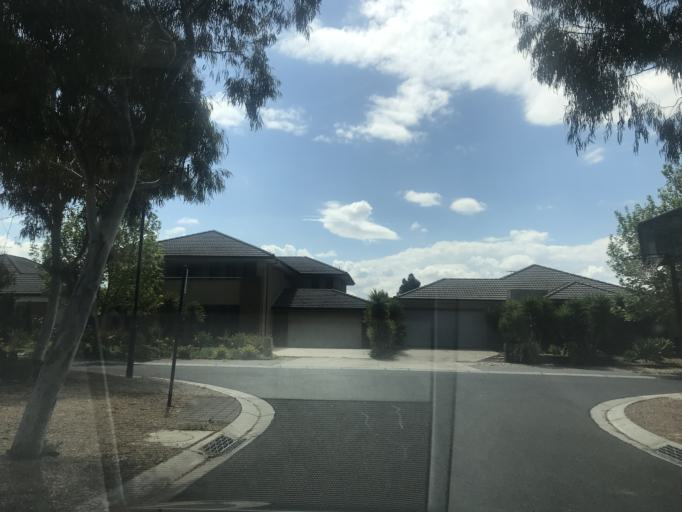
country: AU
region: Victoria
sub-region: Wyndham
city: Williams Landing
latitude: -37.8868
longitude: 144.7316
